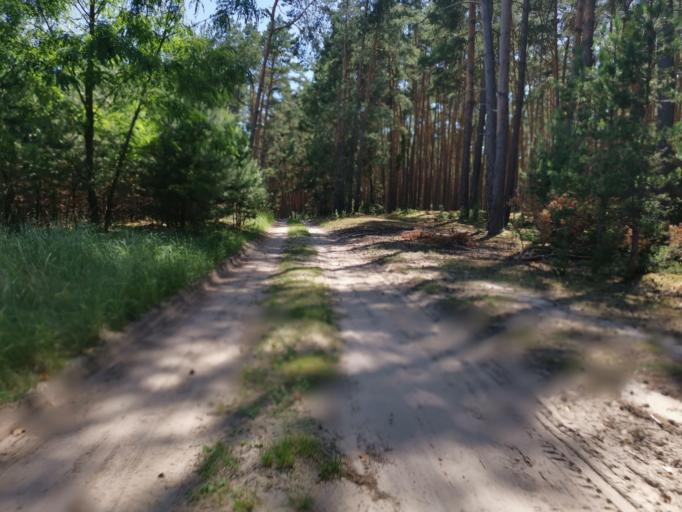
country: CZ
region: South Moravian
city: Vracov
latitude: 48.9634
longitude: 17.2212
